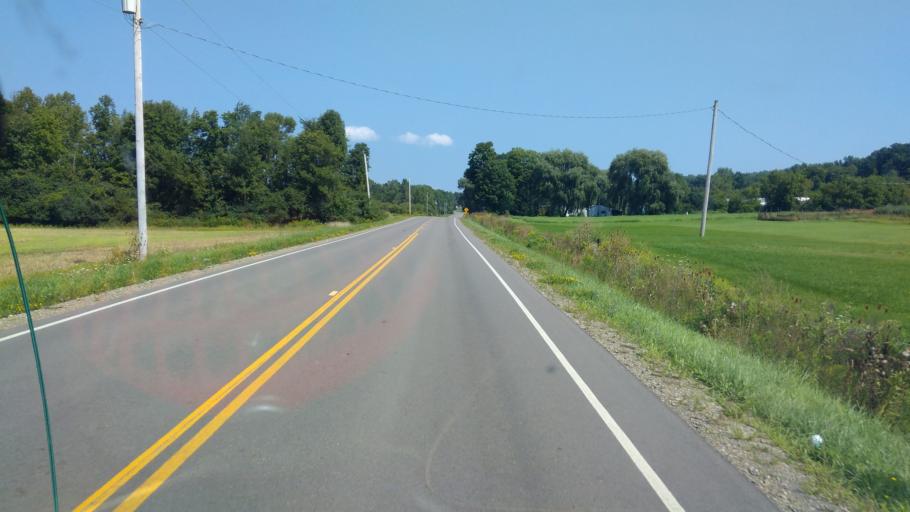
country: US
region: New York
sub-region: Allegany County
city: Belmont
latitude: 42.2536
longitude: -78.0395
